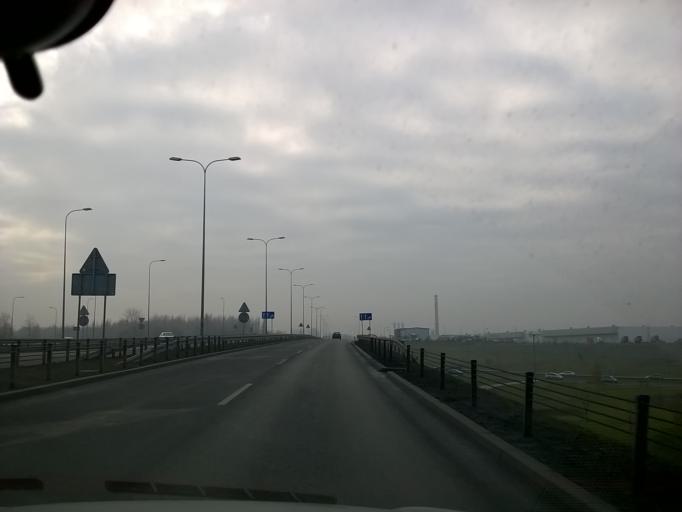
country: PL
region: Silesian Voivodeship
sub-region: Ruda Slaska
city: Ruda Slaska
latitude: 50.2937
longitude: 18.8569
